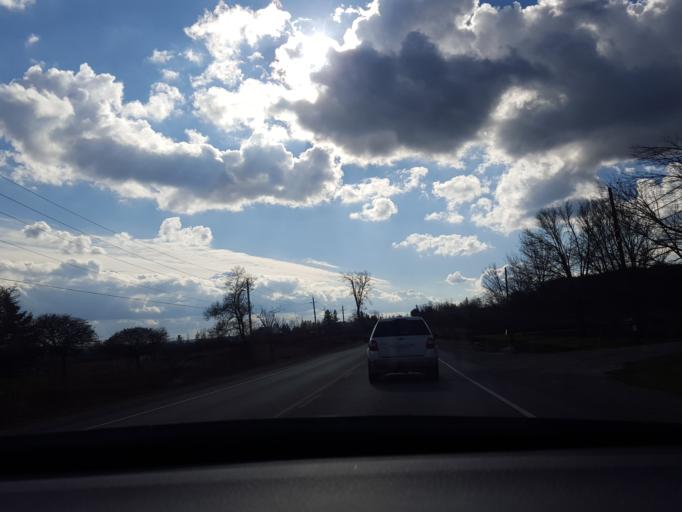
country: CA
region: Ontario
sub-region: Halton
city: Milton
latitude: 43.4812
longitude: -79.8898
